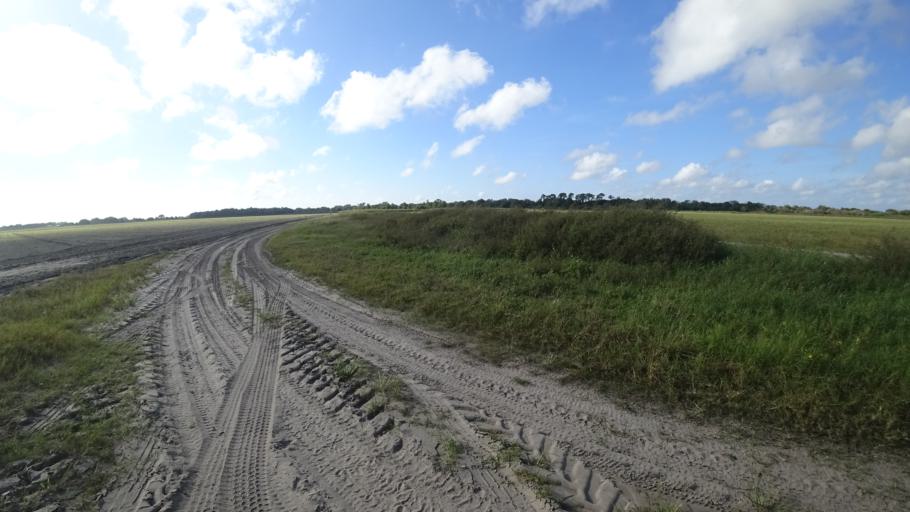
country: US
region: Florida
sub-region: Hillsborough County
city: Wimauma
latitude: 27.5563
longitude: -82.3119
